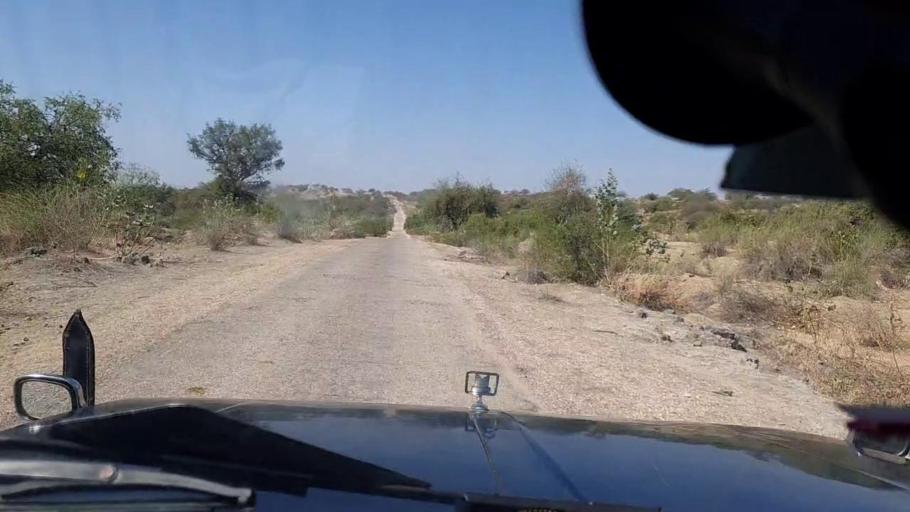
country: PK
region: Sindh
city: Mithi
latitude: 24.6118
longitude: 69.7068
